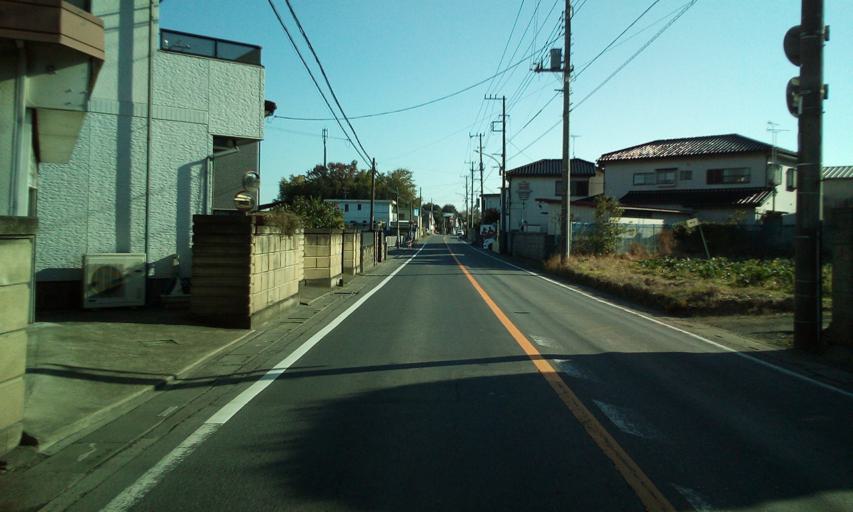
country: JP
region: Chiba
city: Noda
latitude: 35.9533
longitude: 139.8328
